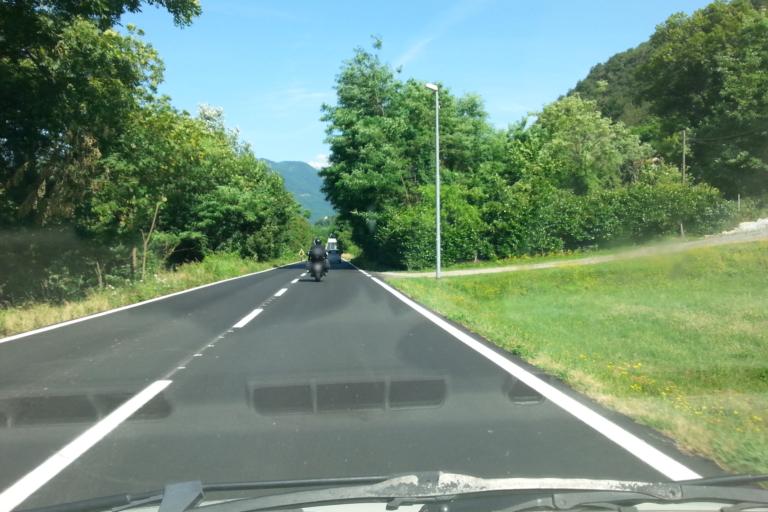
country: IT
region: Piedmont
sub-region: Provincia di Torino
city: Trana
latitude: 45.0430
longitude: 7.4119
